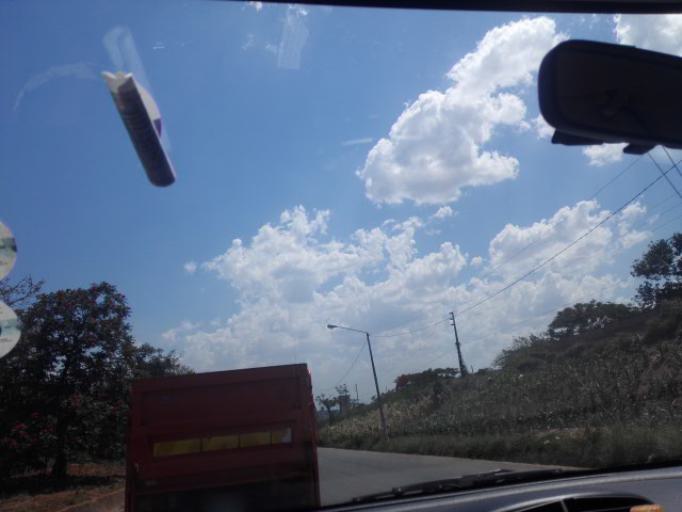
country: MZ
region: Maputo
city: Matola
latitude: -25.9630
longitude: 32.4476
